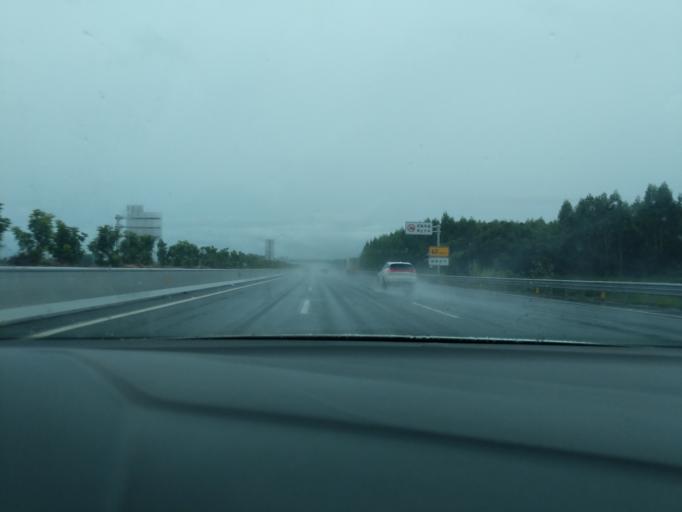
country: CN
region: Guangdong
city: Zhishan
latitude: 22.4843
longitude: 112.7820
